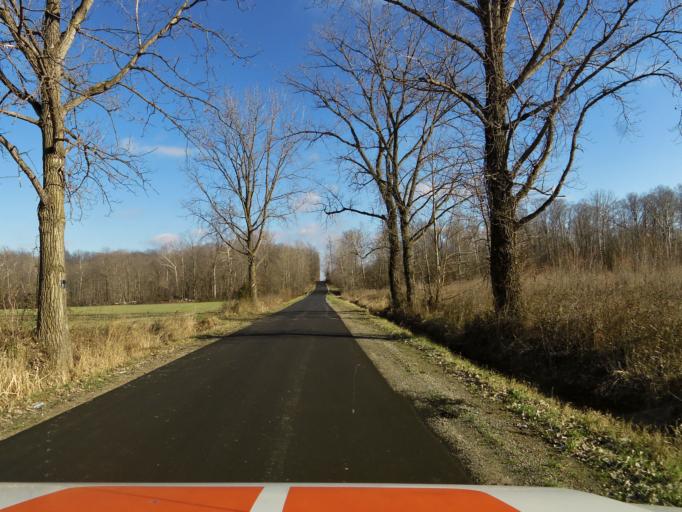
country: US
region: Indiana
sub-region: Jennings County
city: Country Squire Lakes
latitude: 38.9831
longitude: -85.7889
